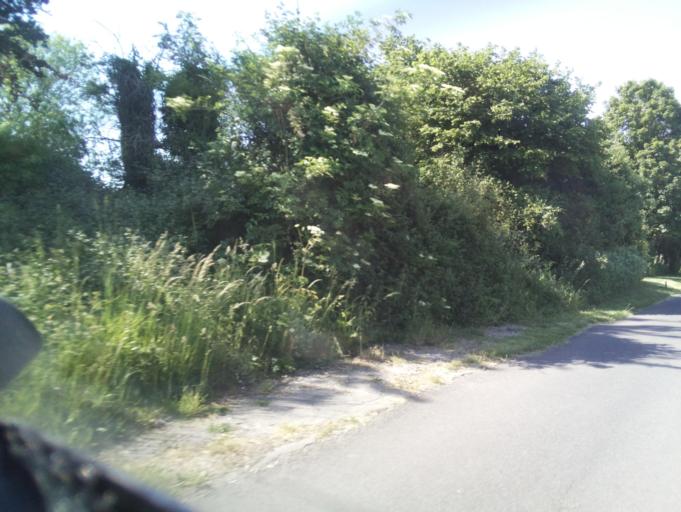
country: GB
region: England
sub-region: Hampshire
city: Abbotts Ann
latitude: 51.2225
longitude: -1.5665
